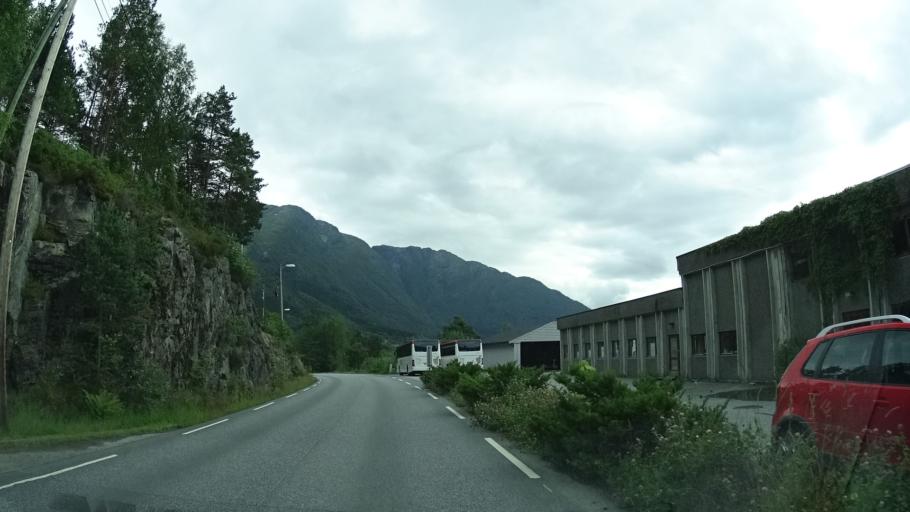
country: NO
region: Hordaland
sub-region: Jondal
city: Jondal
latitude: 60.2854
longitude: 6.2462
